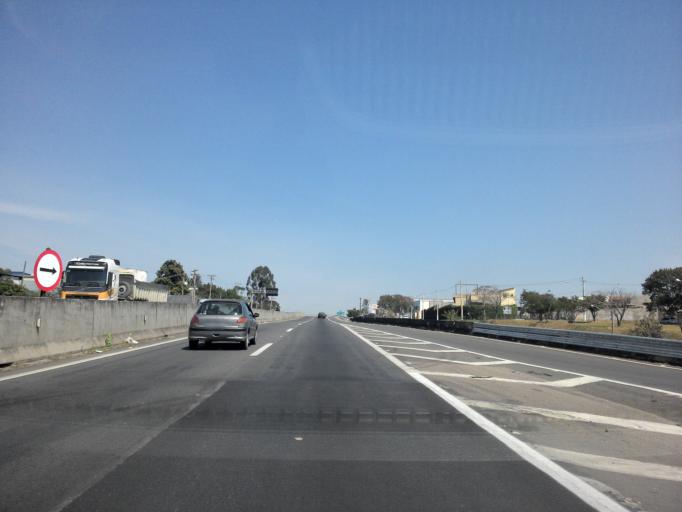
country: BR
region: Sao Paulo
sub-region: Hortolandia
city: Hortolandia
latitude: -22.9046
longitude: -47.2067
